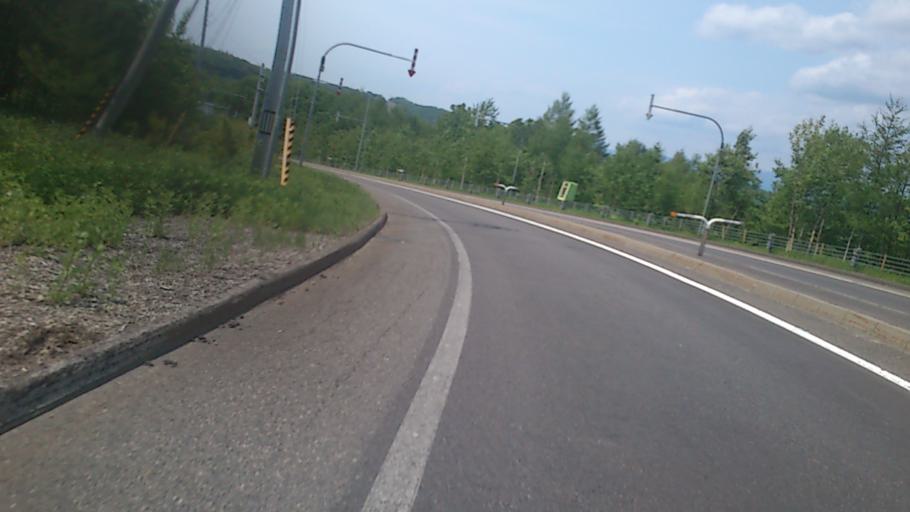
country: JP
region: Hokkaido
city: Otofuke
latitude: 43.2277
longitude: 143.5303
